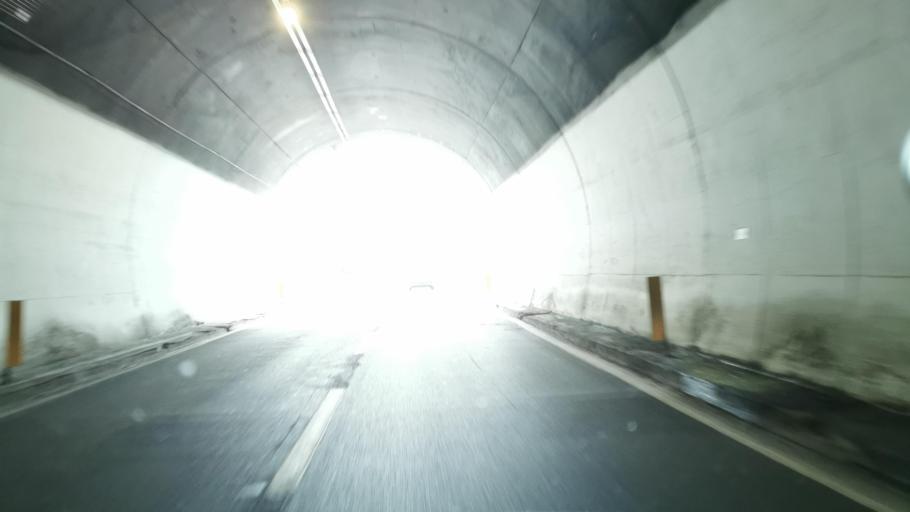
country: IT
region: Piedmont
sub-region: Provincia di Cuneo
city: Bastia Mondovi
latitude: 44.4224
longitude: 7.8793
